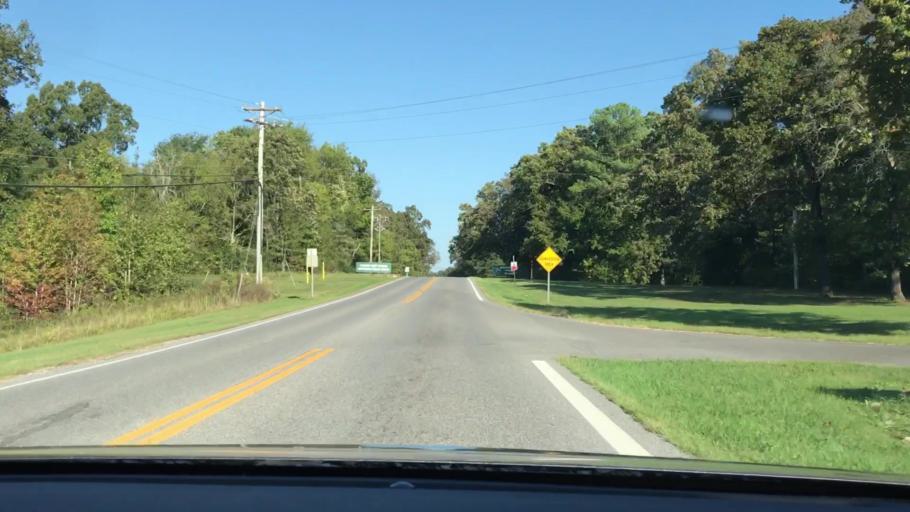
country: US
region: Kentucky
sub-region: Marshall County
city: Benton
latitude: 36.7719
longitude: -88.1383
